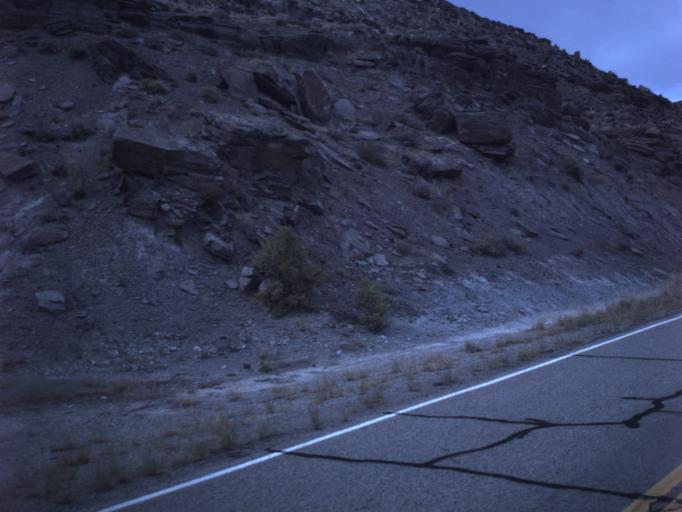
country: US
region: Utah
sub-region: Grand County
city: Moab
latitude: 38.8387
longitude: -109.2861
